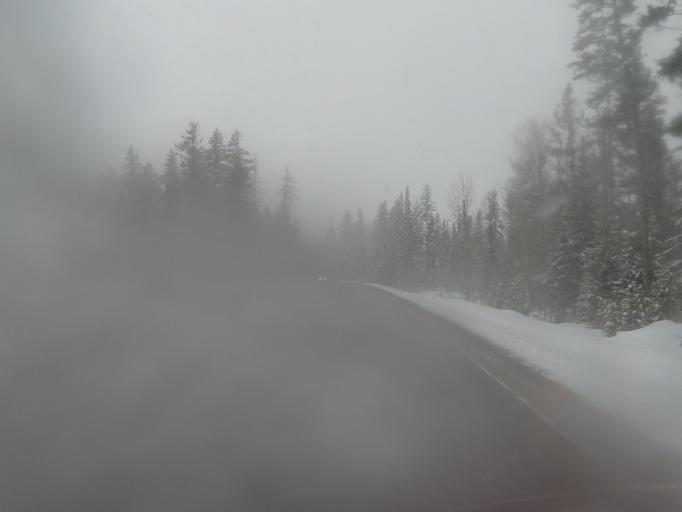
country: US
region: Montana
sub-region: Missoula County
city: Seeley Lake
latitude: 47.4365
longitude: -113.6699
